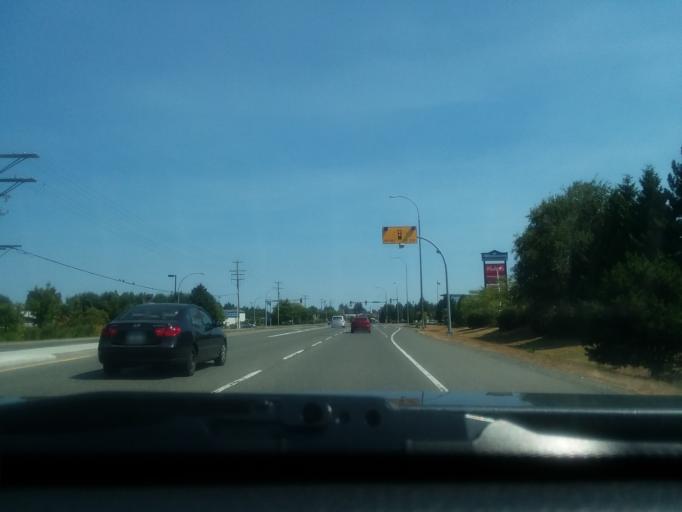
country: CA
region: British Columbia
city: Nanaimo
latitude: 49.2406
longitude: -124.0563
